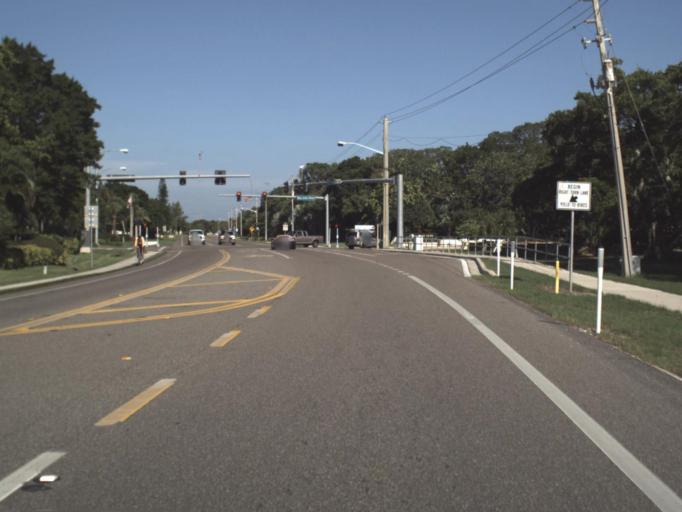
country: US
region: Florida
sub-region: Manatee County
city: Longboat Key
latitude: 27.3647
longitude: -82.6227
